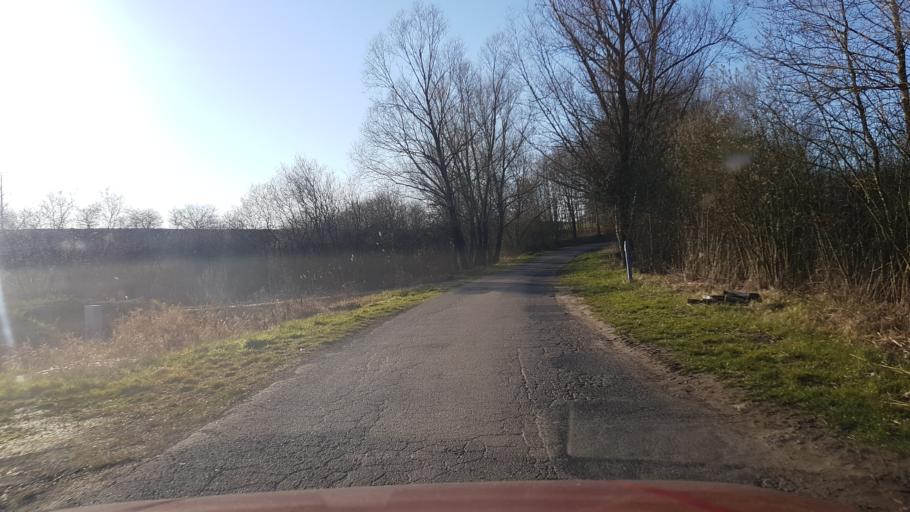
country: PL
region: West Pomeranian Voivodeship
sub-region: Powiat stargardzki
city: Stara Dabrowa
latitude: 53.3821
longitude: 15.0958
